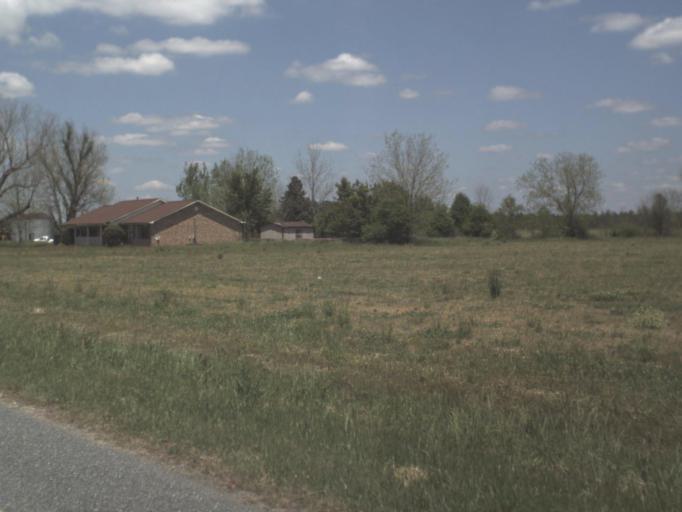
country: US
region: Florida
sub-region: Santa Rosa County
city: Point Baker
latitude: 30.8138
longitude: -87.0447
